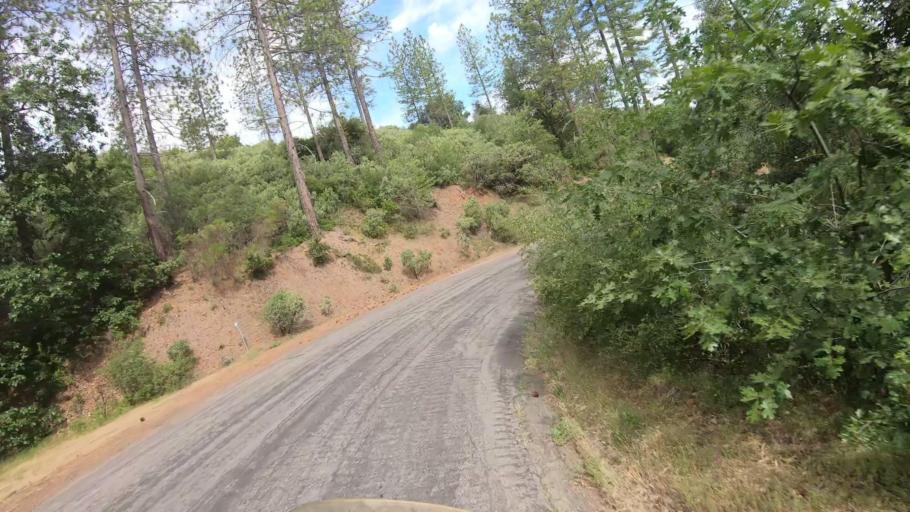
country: US
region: California
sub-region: Tuolumne County
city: Tuolumne City
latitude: 37.8404
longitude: -120.1290
